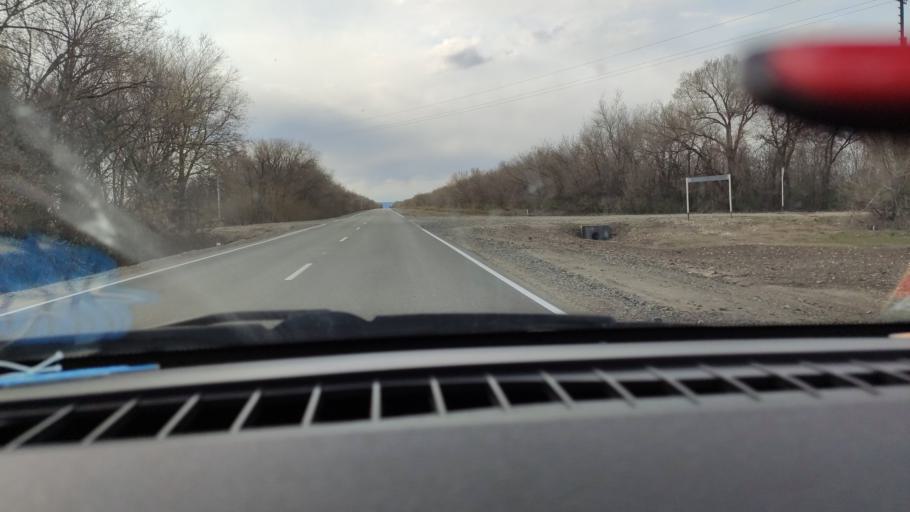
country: RU
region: Saratov
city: Privolzhskiy
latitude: 51.1694
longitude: 45.9407
